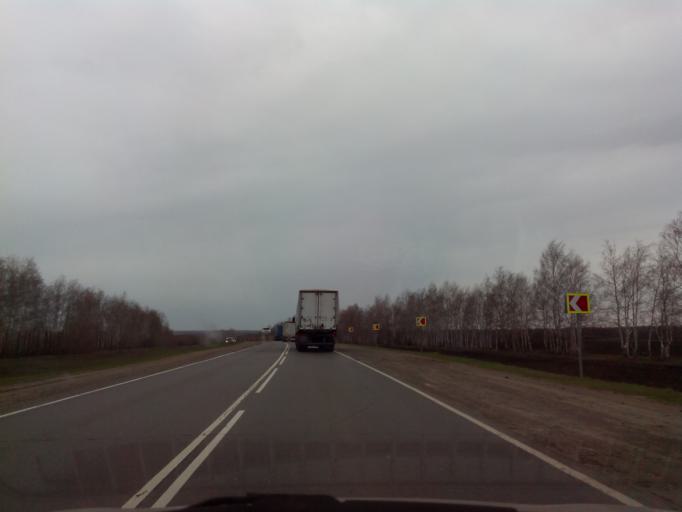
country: RU
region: Tambov
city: Pokrovo-Prigorodnoye
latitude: 52.6681
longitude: 41.3379
